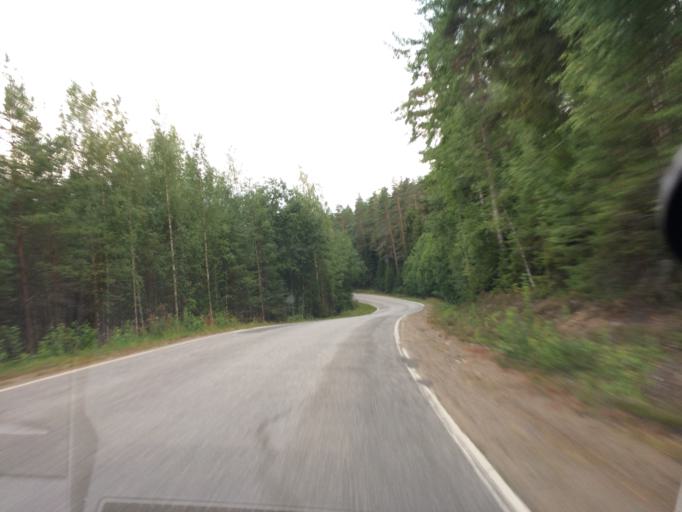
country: FI
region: Haeme
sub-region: Haemeenlinna
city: Tuulos
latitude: 61.2313
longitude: 24.7113
